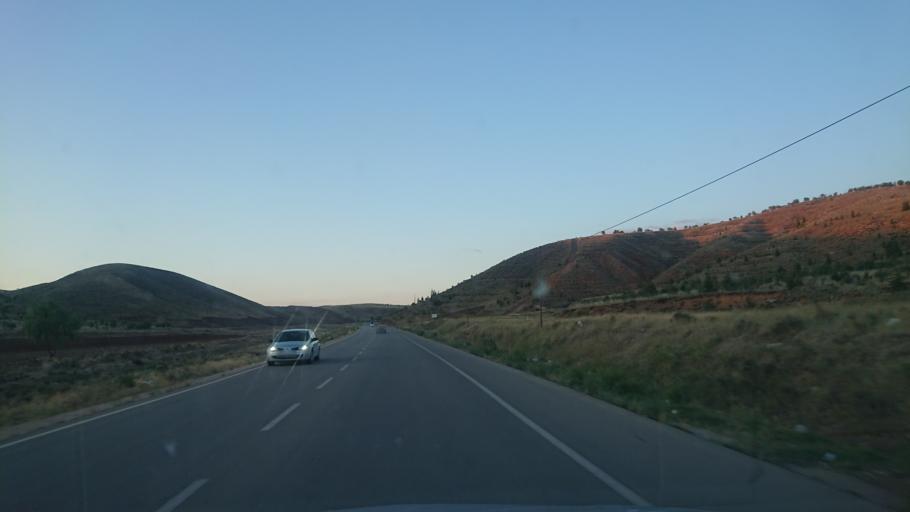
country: TR
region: Aksaray
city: Aksaray
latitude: 38.4190
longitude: 34.0208
